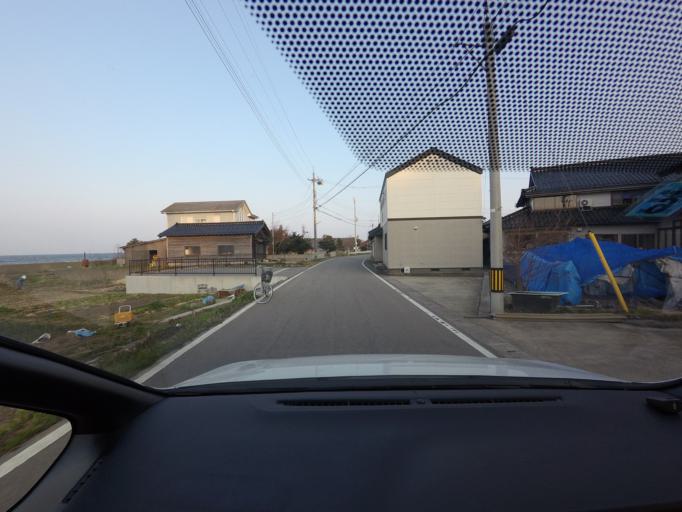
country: JP
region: Ishikawa
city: Nanao
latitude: 37.1567
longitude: 137.0476
